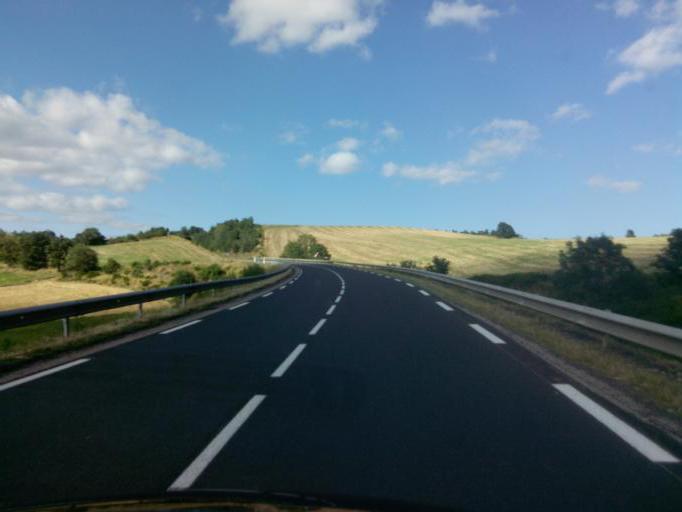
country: FR
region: Auvergne
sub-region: Departement de la Haute-Loire
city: Saint-Paulien
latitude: 45.1612
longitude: 3.8328
